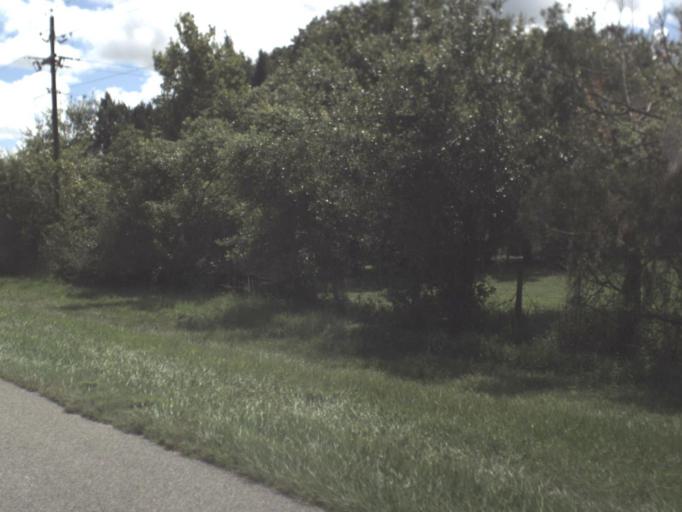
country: US
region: Florida
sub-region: Sarasota County
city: Lake Sarasota
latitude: 27.3612
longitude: -82.1962
